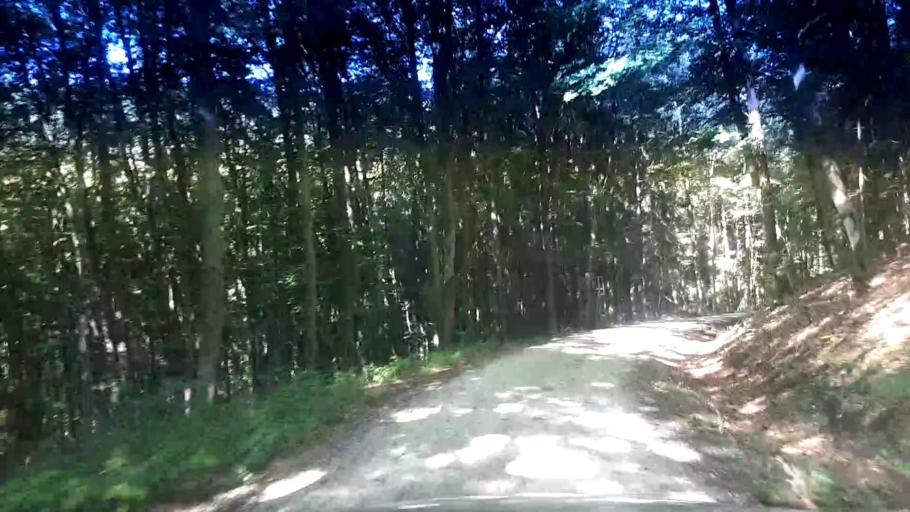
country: DE
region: Bavaria
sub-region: Upper Franconia
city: Litzendorf
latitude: 49.8835
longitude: 11.0337
